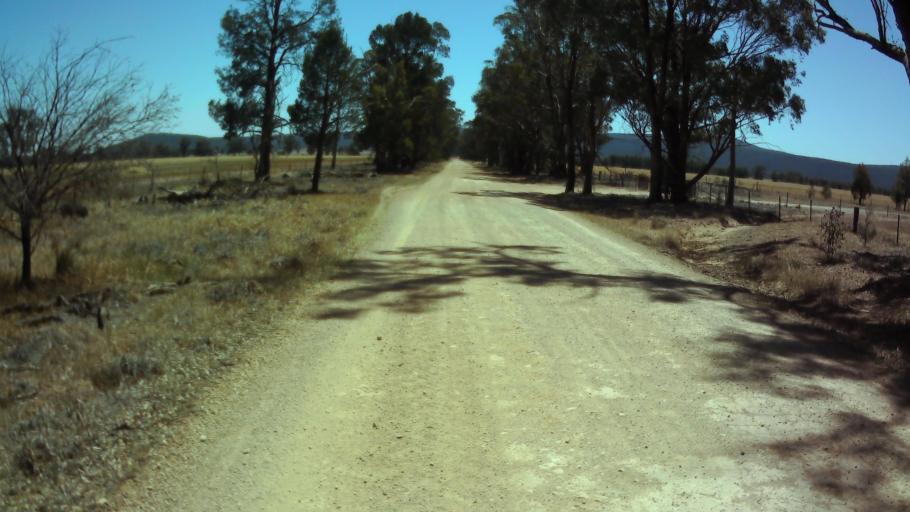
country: AU
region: New South Wales
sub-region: Weddin
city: Grenfell
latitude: -34.0159
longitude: 147.9628
